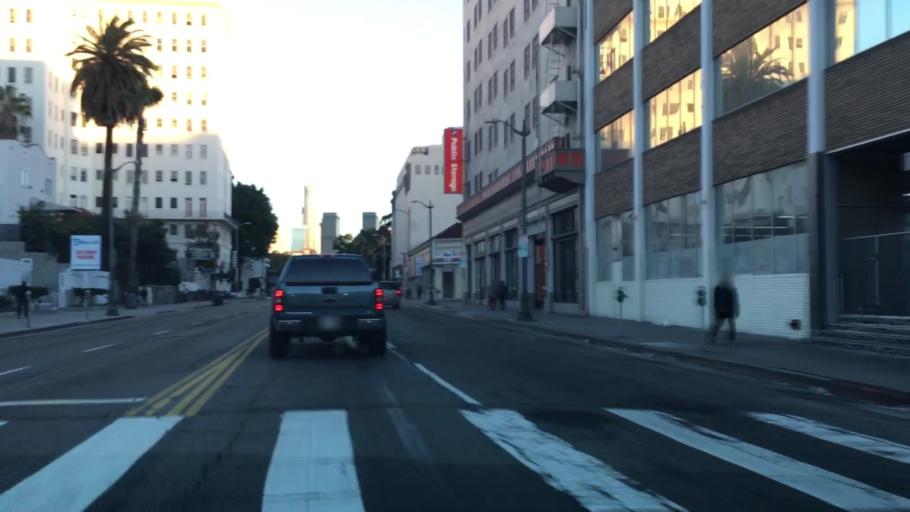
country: US
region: California
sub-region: Los Angeles County
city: Echo Park
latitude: 34.0620
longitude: -118.2803
